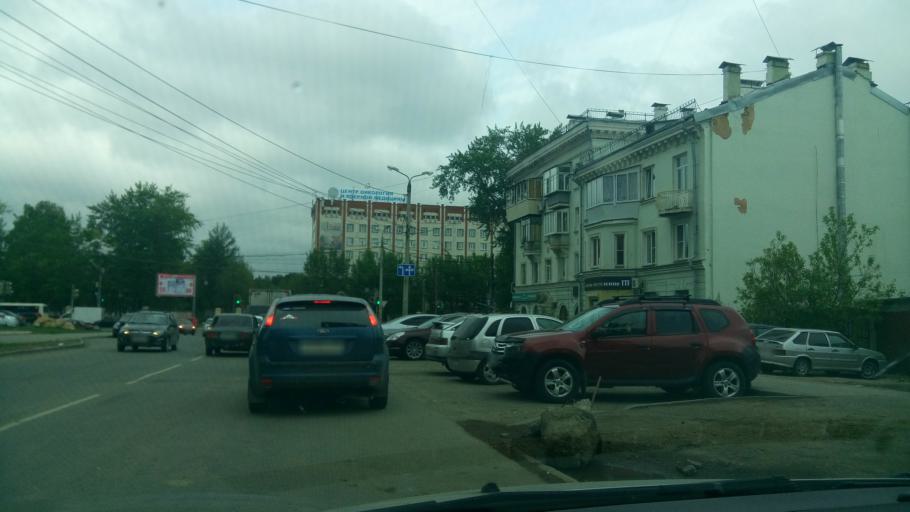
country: RU
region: Chelyabinsk
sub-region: Gorod Chelyabinsk
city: Chelyabinsk
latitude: 55.1322
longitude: 61.3712
